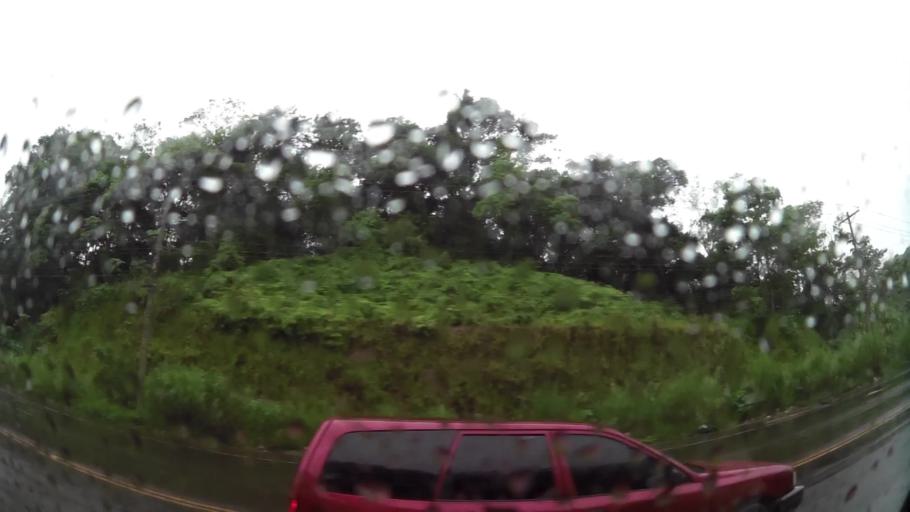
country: PA
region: Colon
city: Santa Rita Arriba
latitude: 9.3295
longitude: -79.8017
